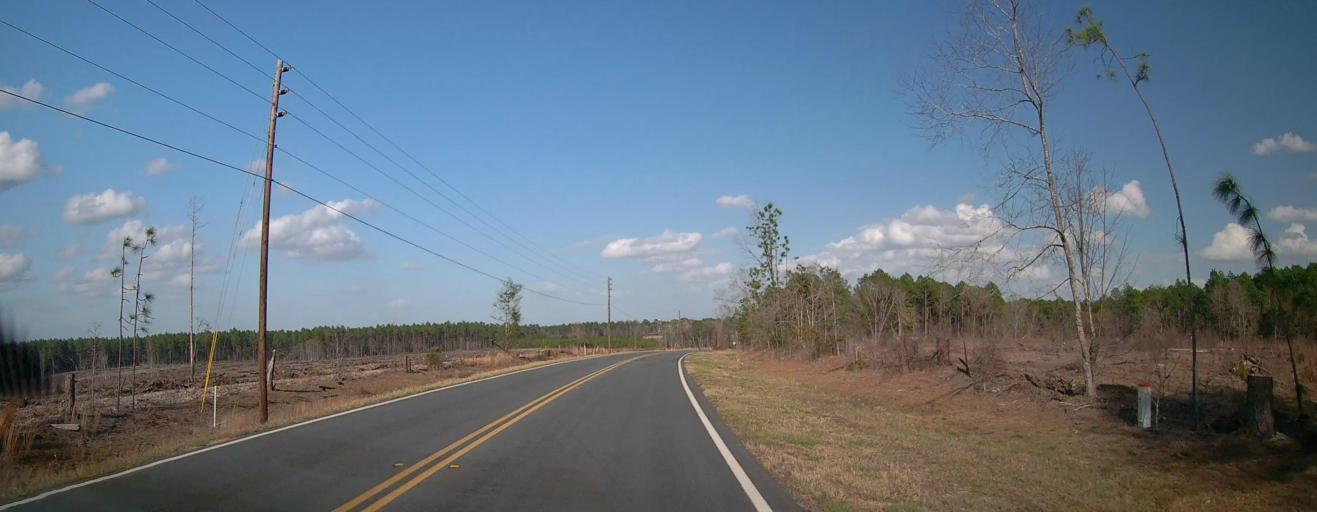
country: US
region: Georgia
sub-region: Telfair County
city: McRae
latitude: 32.0405
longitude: -82.8344
